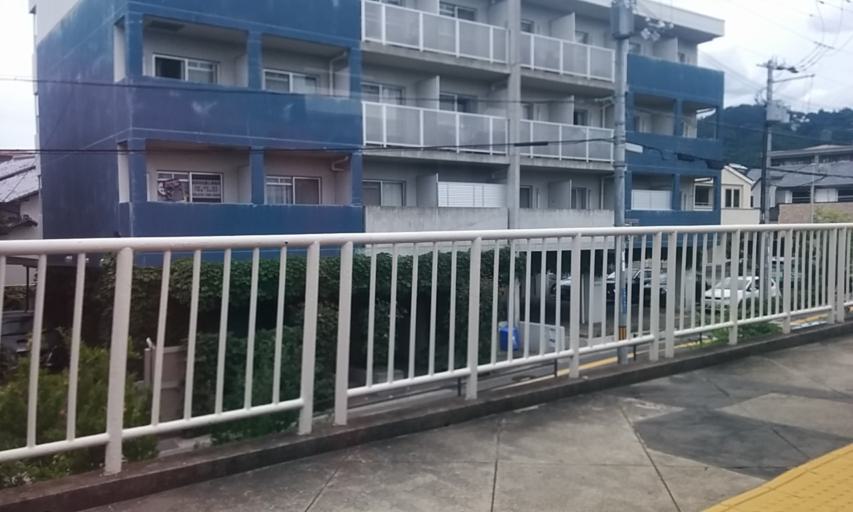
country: JP
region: Osaka
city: Mino
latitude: 34.8236
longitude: 135.4658
